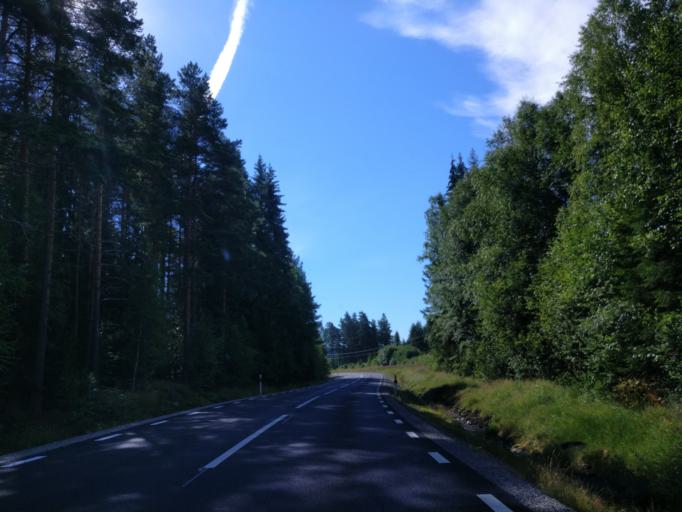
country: SE
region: Vaermland
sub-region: Hagfors Kommun
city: Hagfors
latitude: 60.0382
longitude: 13.8252
